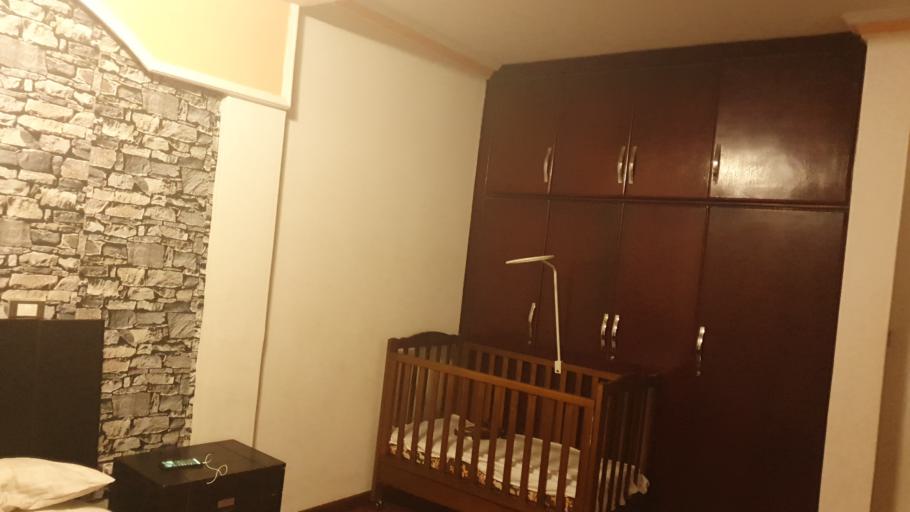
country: ET
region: Adis Abeba
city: Addis Ababa
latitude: 8.9574
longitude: 38.7226
